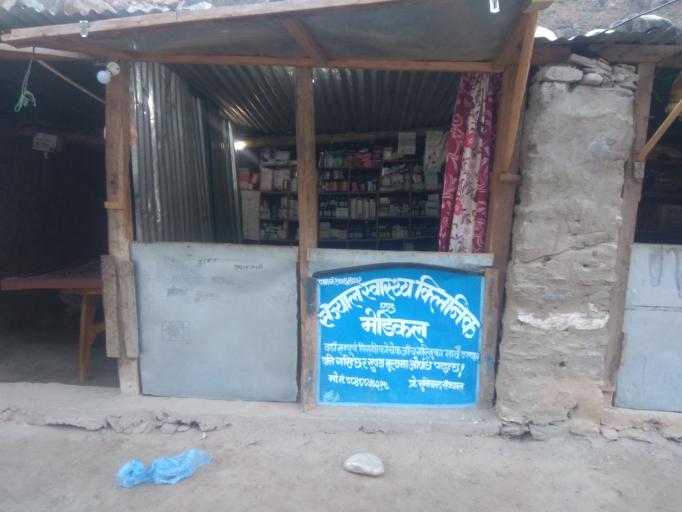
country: NP
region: Mid Western
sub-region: Bheri Zone
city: Dailekh
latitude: 29.2747
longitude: 81.7260
